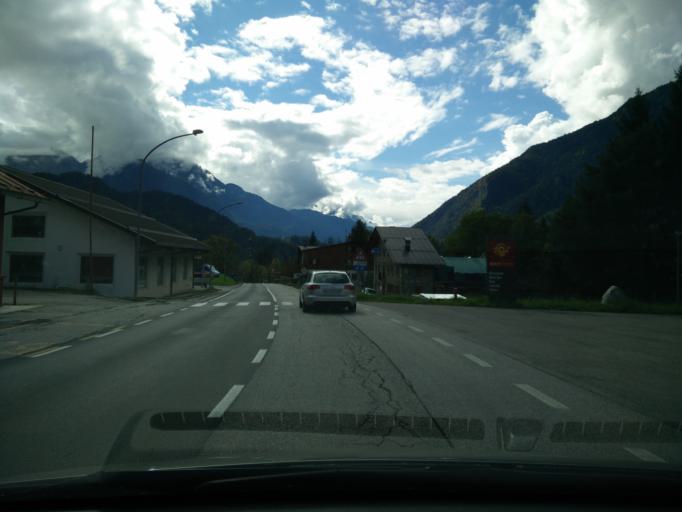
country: IT
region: Veneto
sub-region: Provincia di Belluno
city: Vigo di Cadore
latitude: 46.5163
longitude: 12.4641
